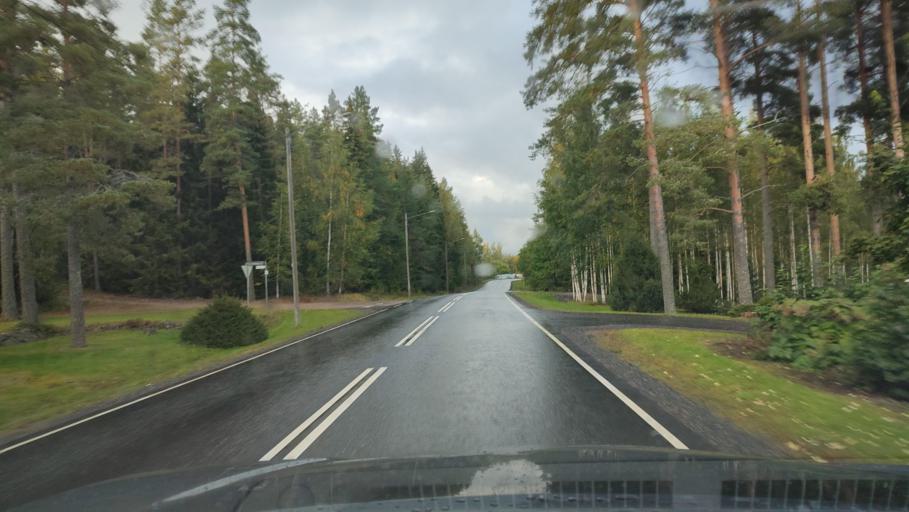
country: FI
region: Southern Ostrobothnia
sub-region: Suupohja
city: Karijoki
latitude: 62.2985
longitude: 21.6831
